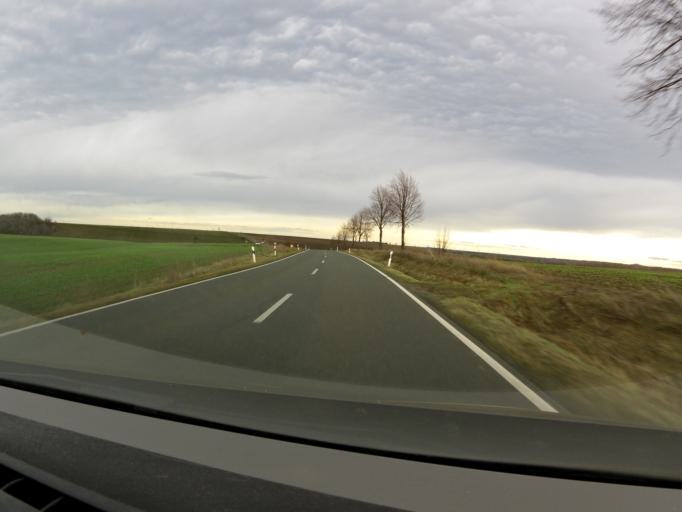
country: DE
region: Saxony-Anhalt
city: Belleben
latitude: 51.6889
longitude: 11.6416
